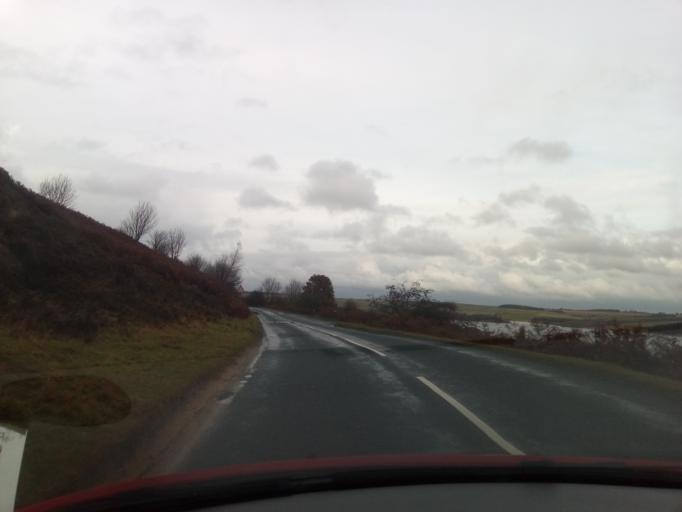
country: GB
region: England
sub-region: County Durham
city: Muggleswick
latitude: 54.8515
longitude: -1.9805
